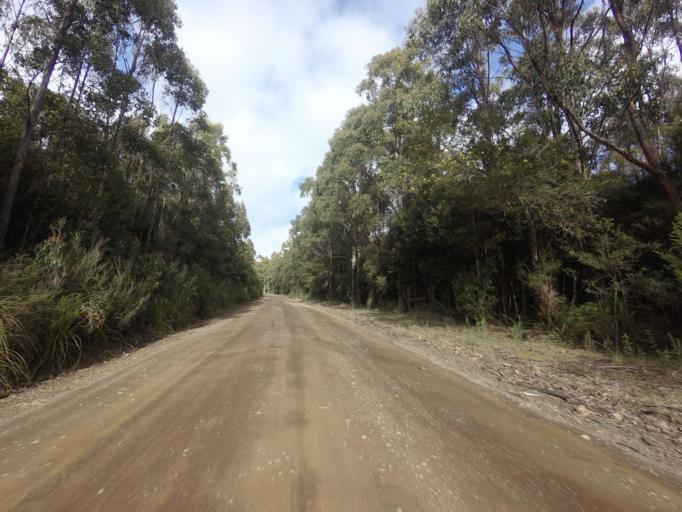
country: AU
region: Tasmania
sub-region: Huon Valley
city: Geeveston
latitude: -43.4683
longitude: 146.8938
